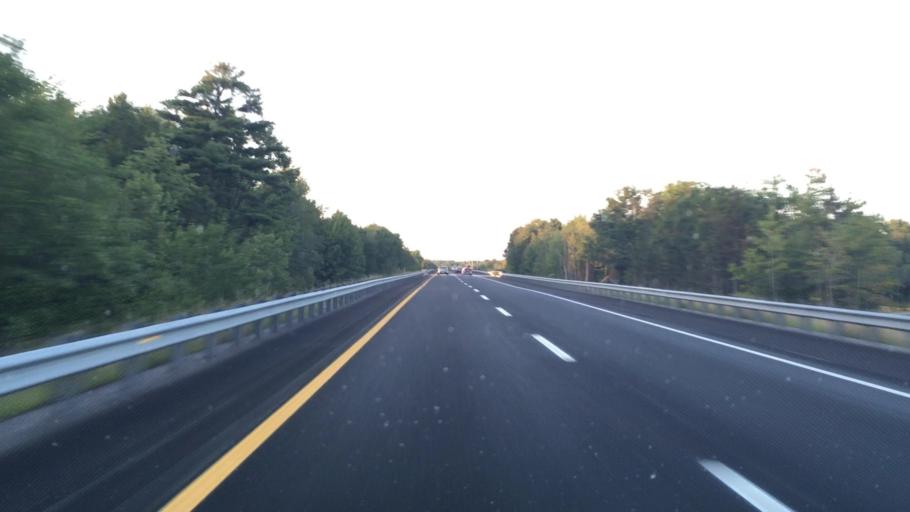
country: US
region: Maine
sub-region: Sagadahoc County
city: Topsham
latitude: 44.0158
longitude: -69.9200
